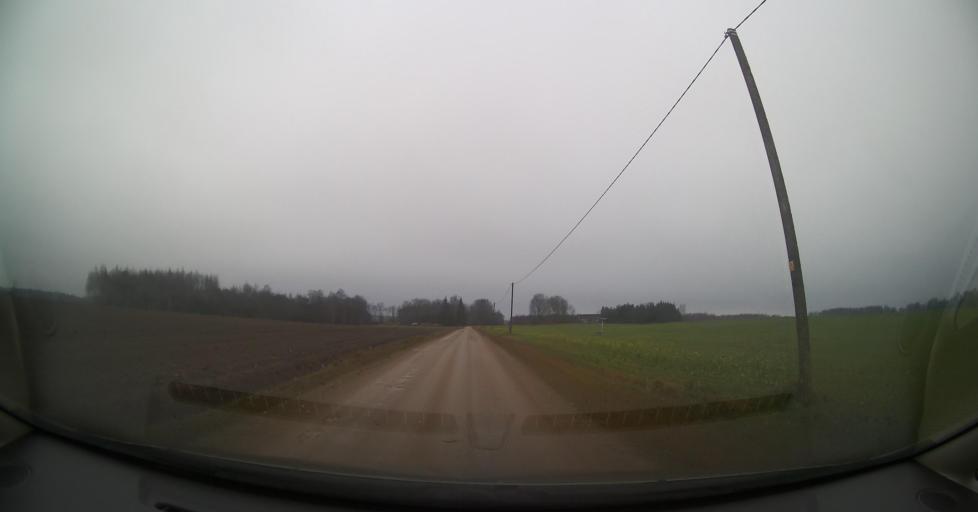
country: EE
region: Tartu
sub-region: Tartu linn
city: Tartu
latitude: 58.3931
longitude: 27.0071
